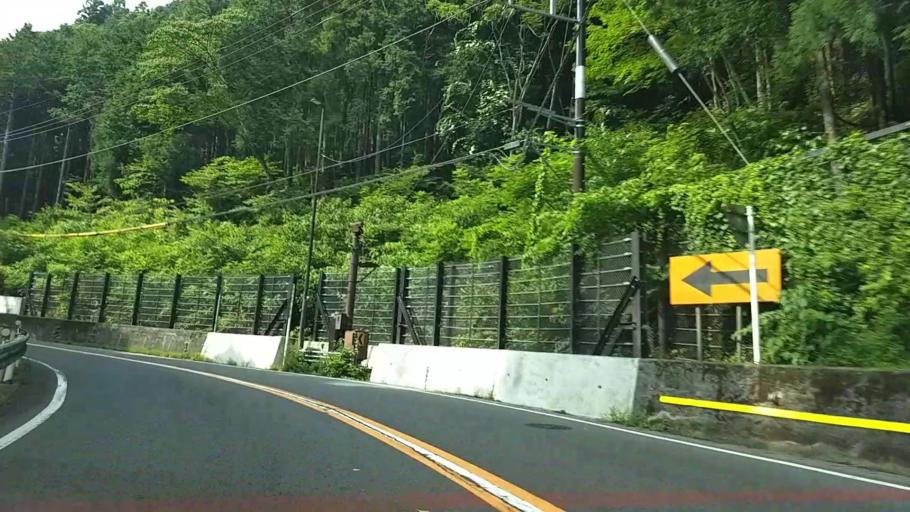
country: JP
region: Tokyo
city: Hachioji
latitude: 35.6200
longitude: 139.2372
